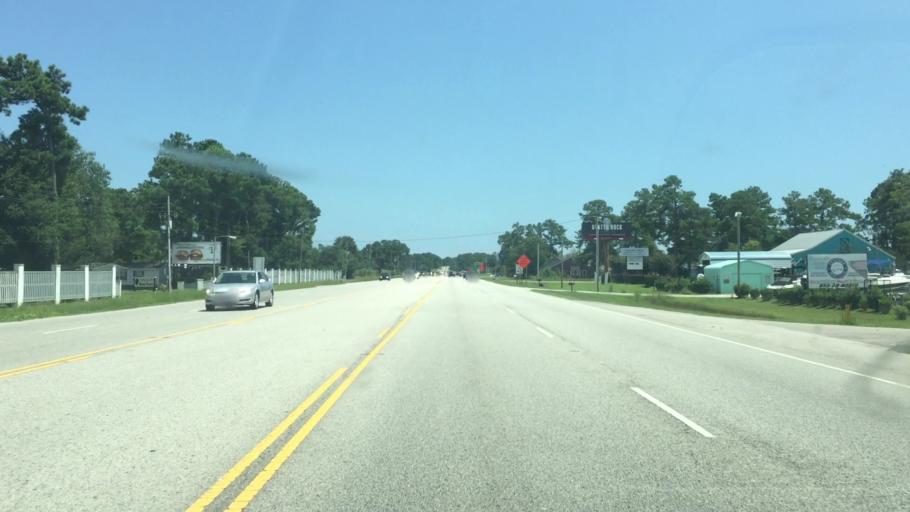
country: US
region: South Carolina
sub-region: Horry County
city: North Myrtle Beach
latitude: 33.8706
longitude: -78.6708
